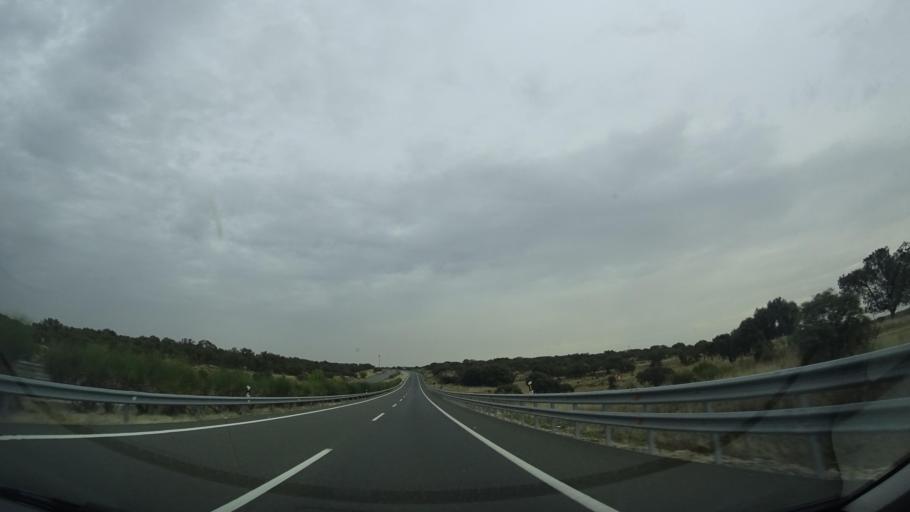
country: ES
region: Extremadura
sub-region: Provincia de Caceres
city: Jaraicejo
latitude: 39.6124
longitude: -5.8309
